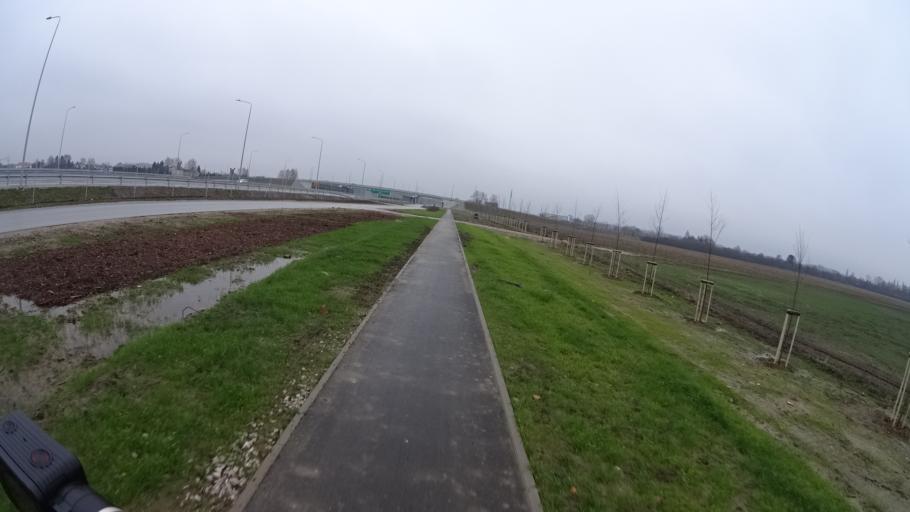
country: PL
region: Masovian Voivodeship
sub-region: Warszawa
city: Wilanow
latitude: 52.1548
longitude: 21.1189
